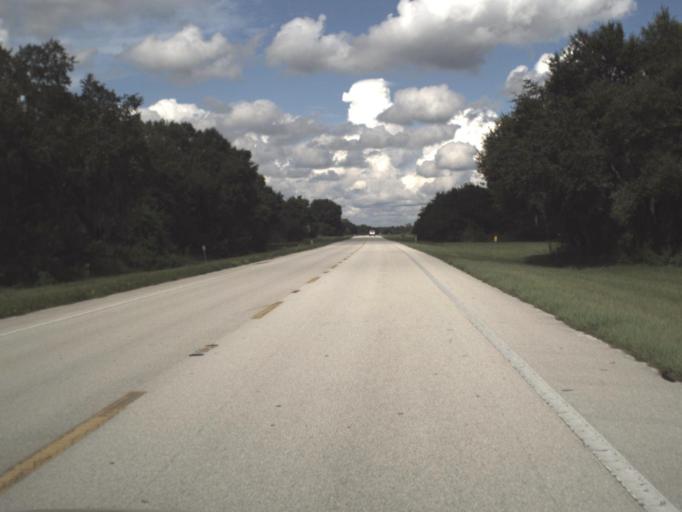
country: US
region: Florida
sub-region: Hillsborough County
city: Ruskin
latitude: 27.6329
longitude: -82.3975
